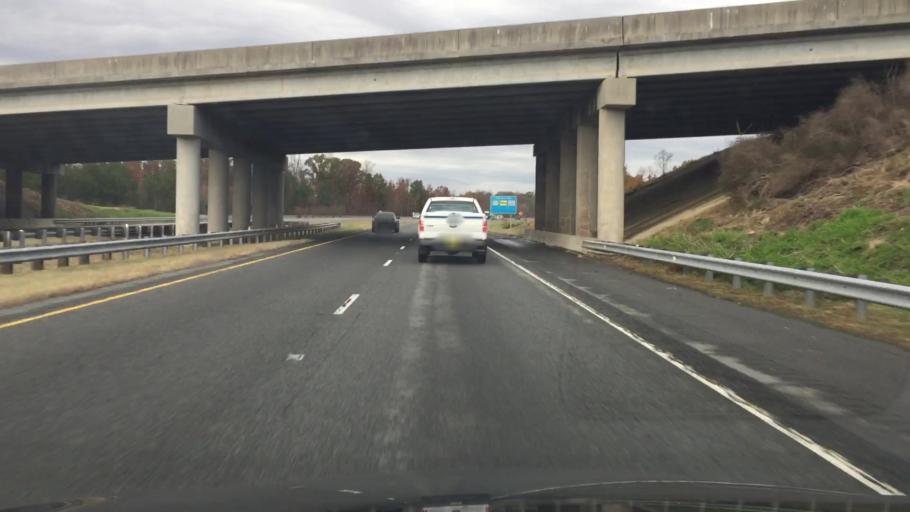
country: US
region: North Carolina
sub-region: Rockingham County
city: Reidsville
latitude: 36.3114
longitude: -79.6450
